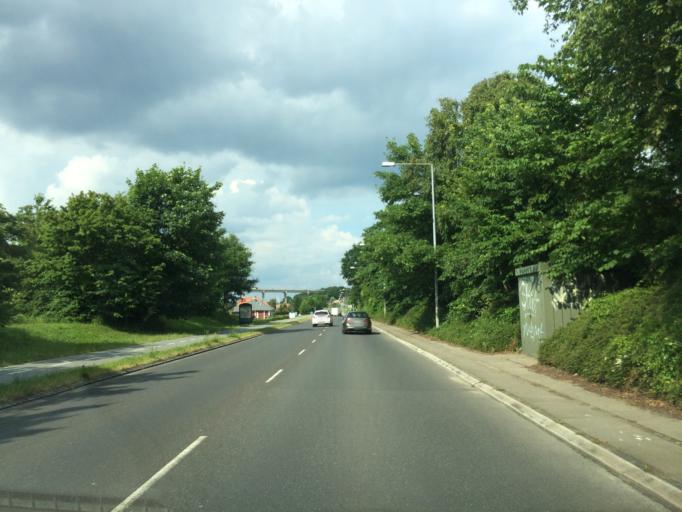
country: DK
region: South Denmark
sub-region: Middelfart Kommune
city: Middelfart
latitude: 55.5095
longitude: 9.7547
